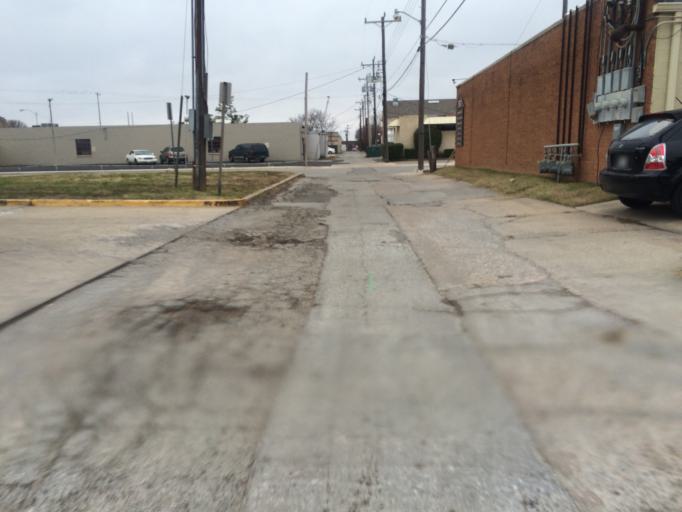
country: US
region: Oklahoma
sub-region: Cleveland County
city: Norman
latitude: 35.2232
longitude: -97.4424
